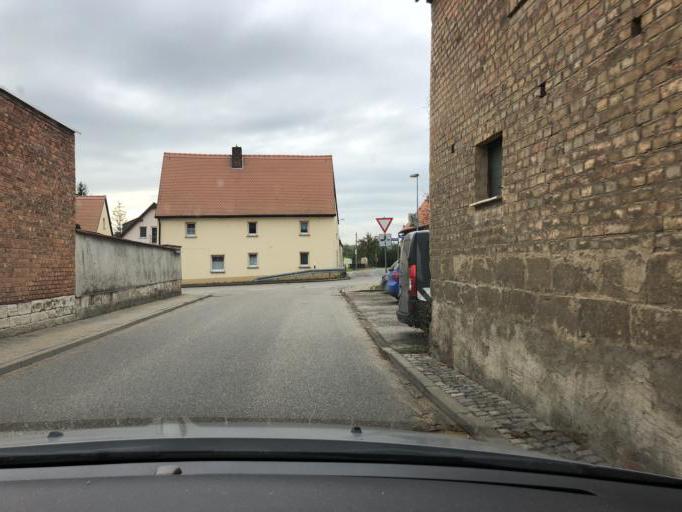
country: DE
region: Saxony-Anhalt
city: Uichteritz
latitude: 51.2154
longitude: 11.9406
